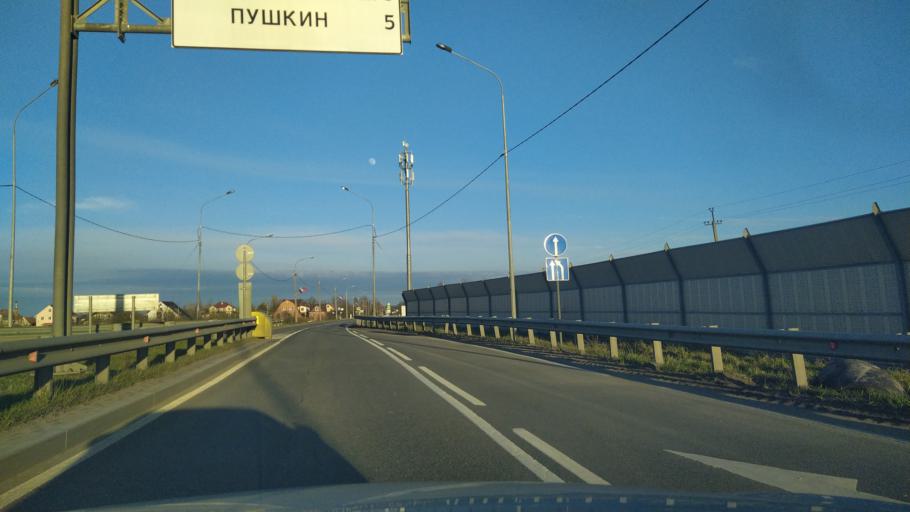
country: RU
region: St.-Petersburg
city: Aleksandrovskaya
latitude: 59.7399
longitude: 30.3212
